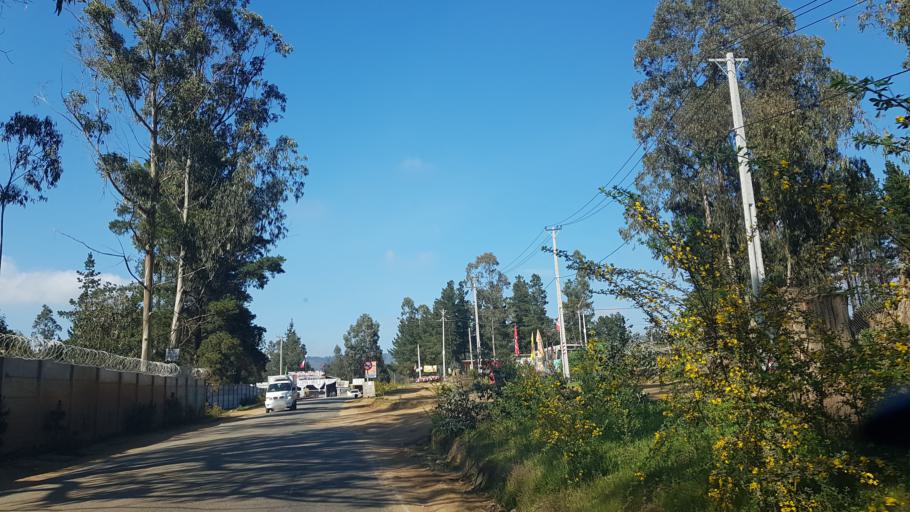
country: CL
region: Valparaiso
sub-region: Provincia de Valparaiso
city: Valparaiso
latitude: -33.1253
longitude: -71.6682
